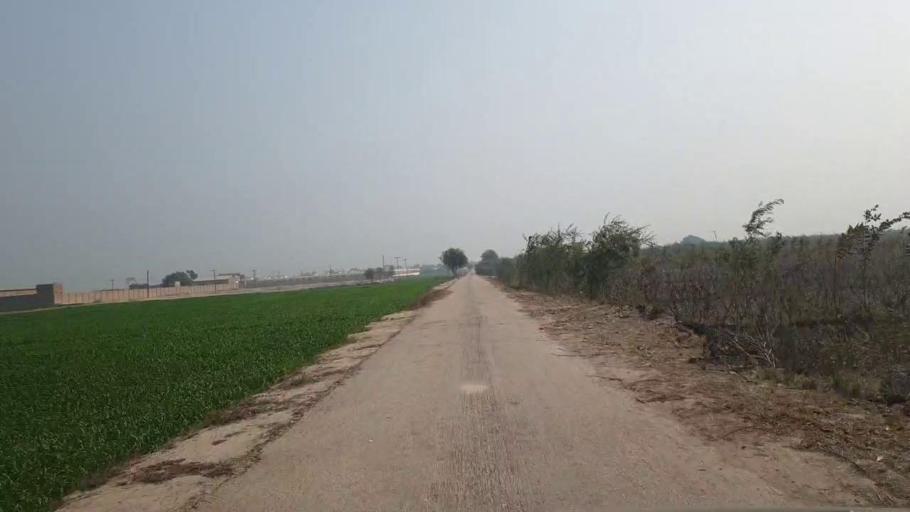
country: PK
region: Sindh
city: Hala
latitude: 25.8253
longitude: 68.4391
